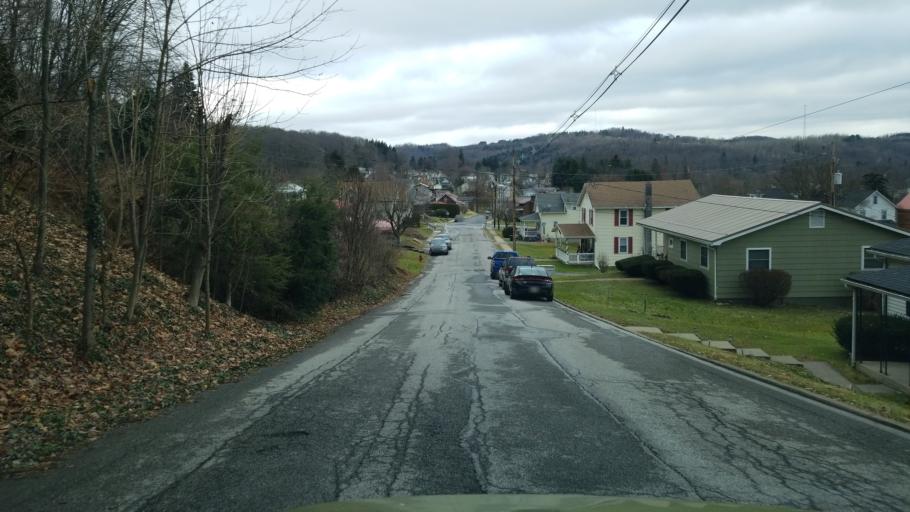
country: US
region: Pennsylvania
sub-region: Clearfield County
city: Clearfield
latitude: 41.0259
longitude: -78.4514
